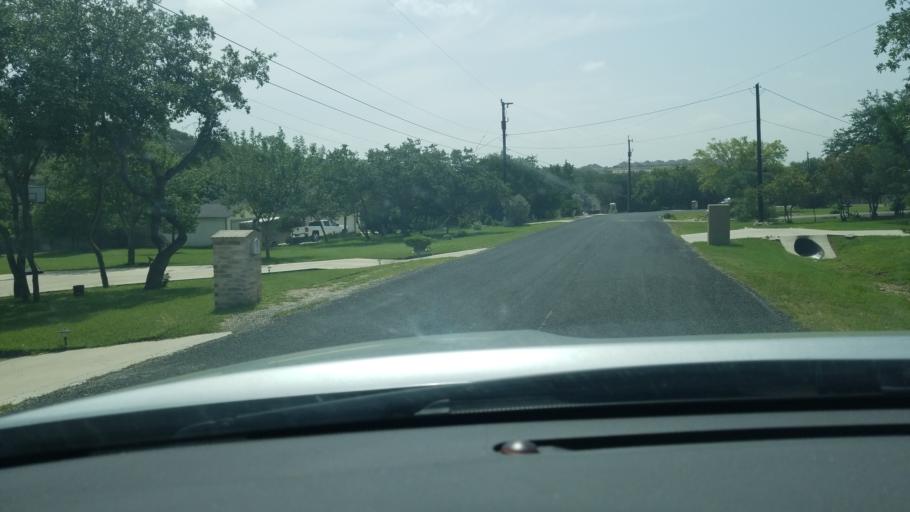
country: US
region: Texas
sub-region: Bexar County
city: Timberwood Park
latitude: 29.6867
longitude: -98.4894
